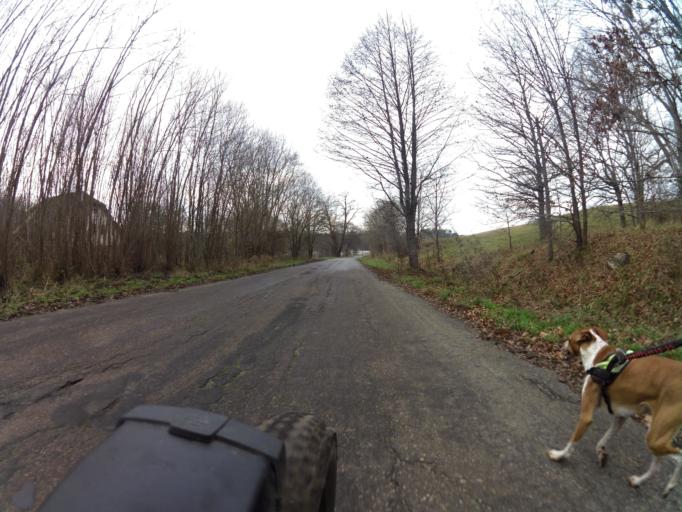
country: PL
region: West Pomeranian Voivodeship
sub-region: Powiat koszalinski
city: Polanow
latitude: 54.0653
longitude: 16.6578
